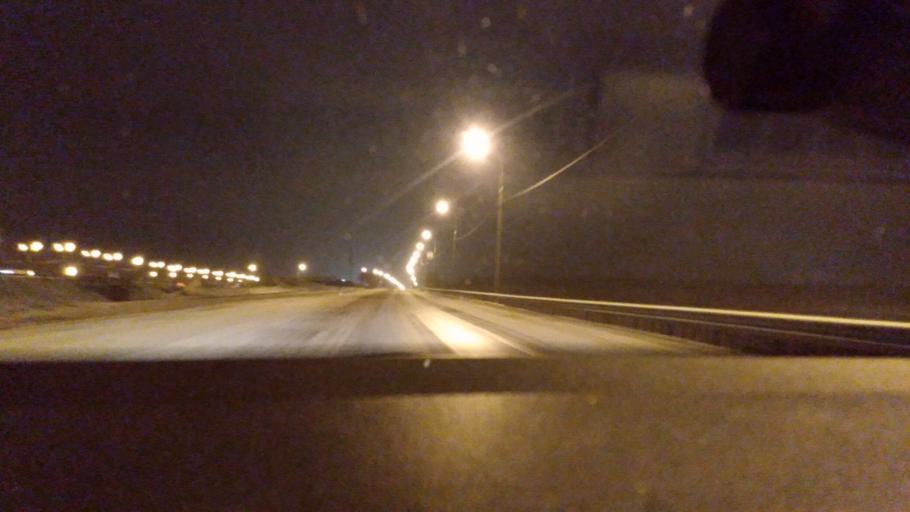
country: RU
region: Moskovskaya
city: Raduzhnyy
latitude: 55.1549
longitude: 38.6949
